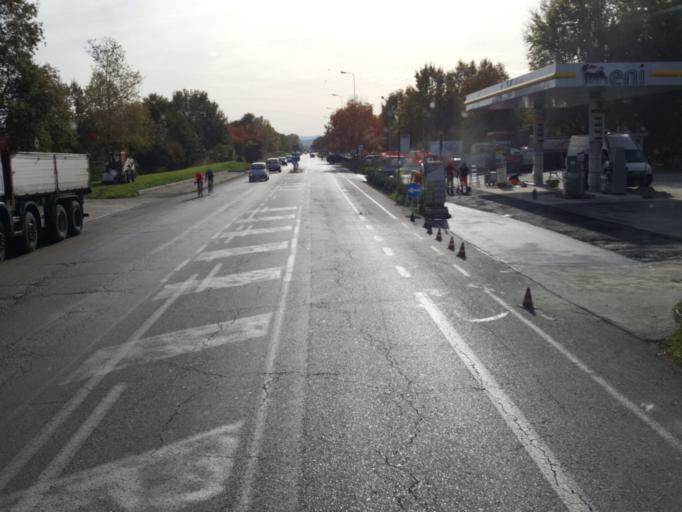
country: IT
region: Emilia-Romagna
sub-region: Provincia di Ravenna
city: Faenza
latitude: 44.3187
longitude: 11.9031
